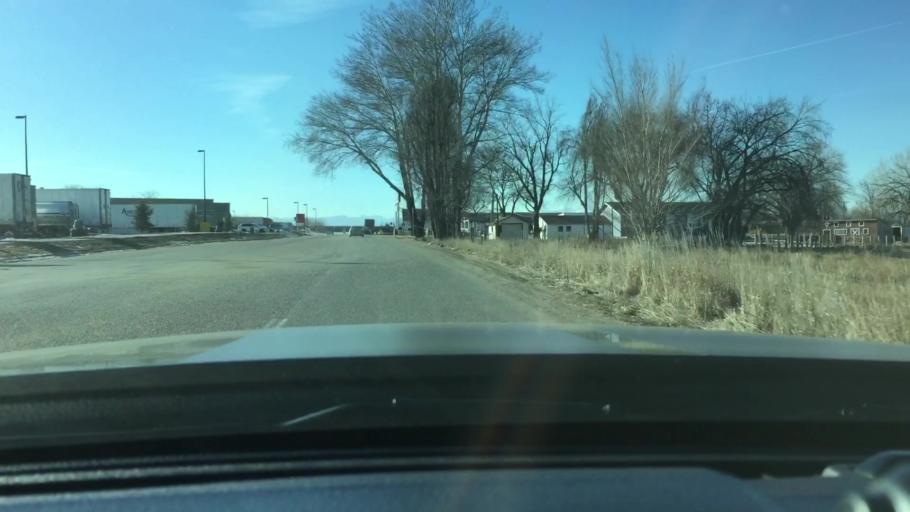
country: US
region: Colorado
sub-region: Weld County
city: Johnstown
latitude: 40.3637
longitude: -104.9815
